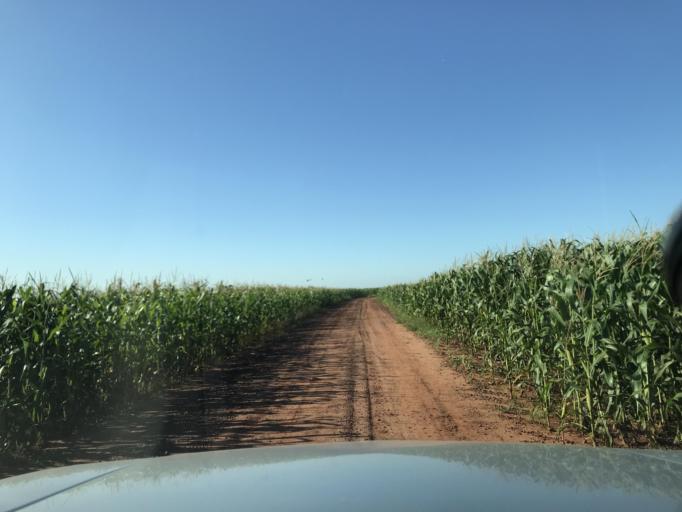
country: BR
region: Parana
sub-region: Palotina
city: Palotina
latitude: -24.2360
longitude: -53.7722
